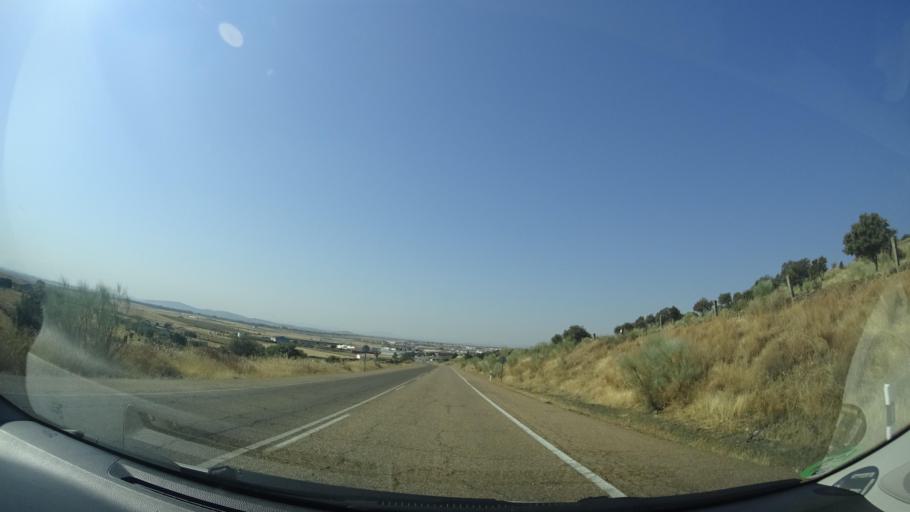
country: ES
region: Extremadura
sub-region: Provincia de Caceres
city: Escurial
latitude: 39.1656
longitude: -5.8986
